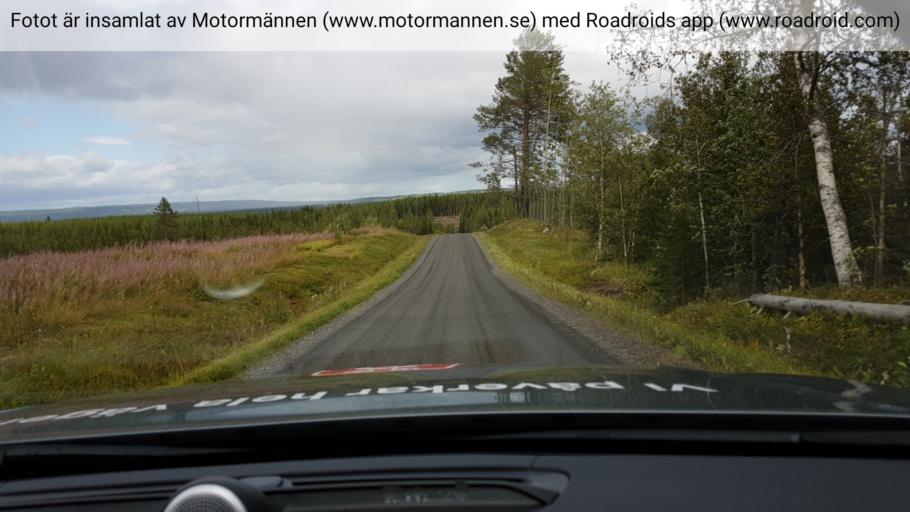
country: SE
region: Jaemtland
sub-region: OEstersunds Kommun
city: Lit
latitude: 63.7435
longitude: 14.6442
